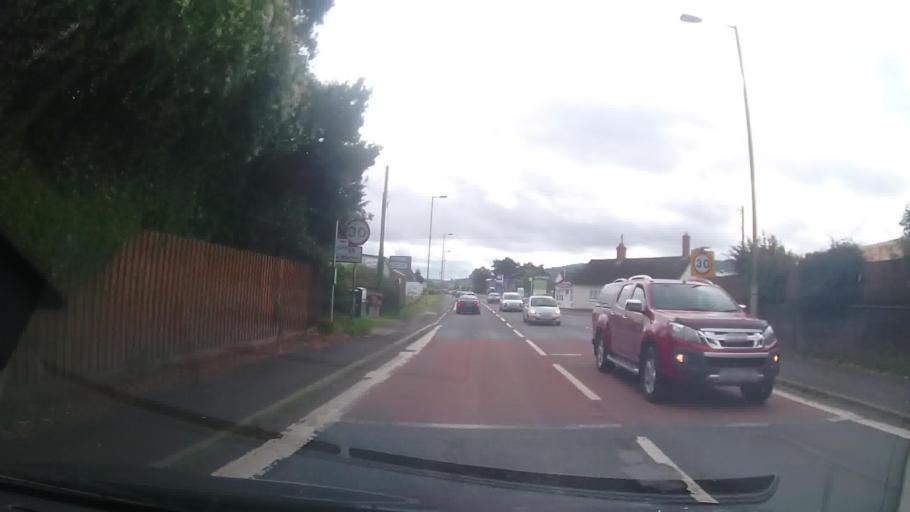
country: GB
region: England
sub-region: Shropshire
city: Craven Arms
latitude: 52.4473
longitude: -2.8376
